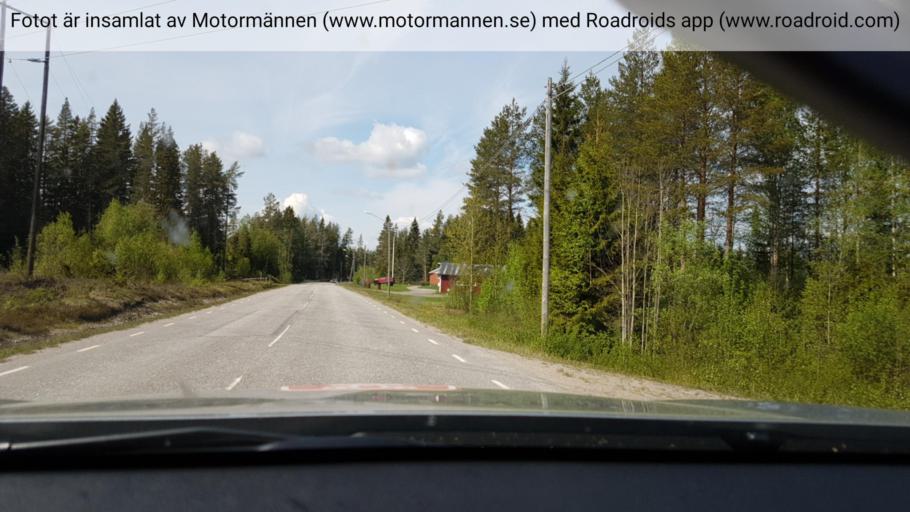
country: SE
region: Vaesterbotten
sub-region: Umea Kommun
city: Roback
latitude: 63.8563
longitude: 20.0813
